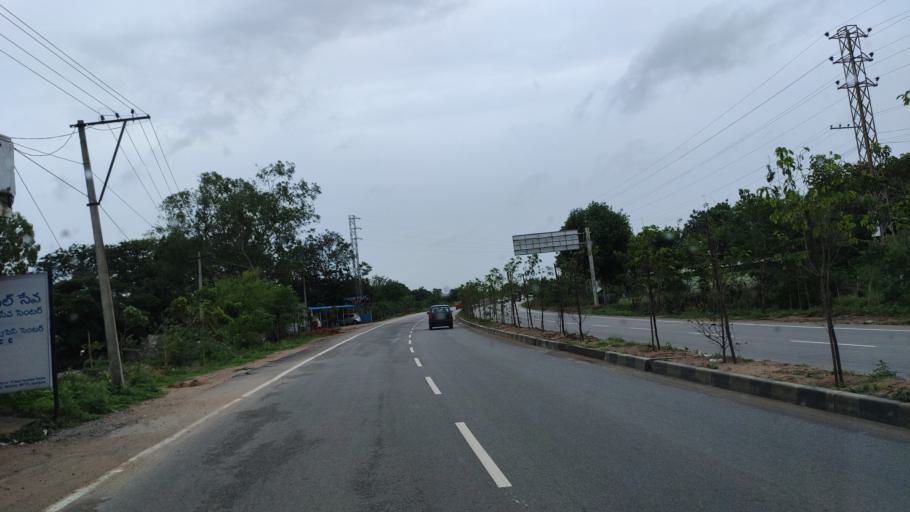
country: IN
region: Telangana
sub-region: Rangareddi
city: Secunderabad
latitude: 17.6003
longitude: 78.5678
